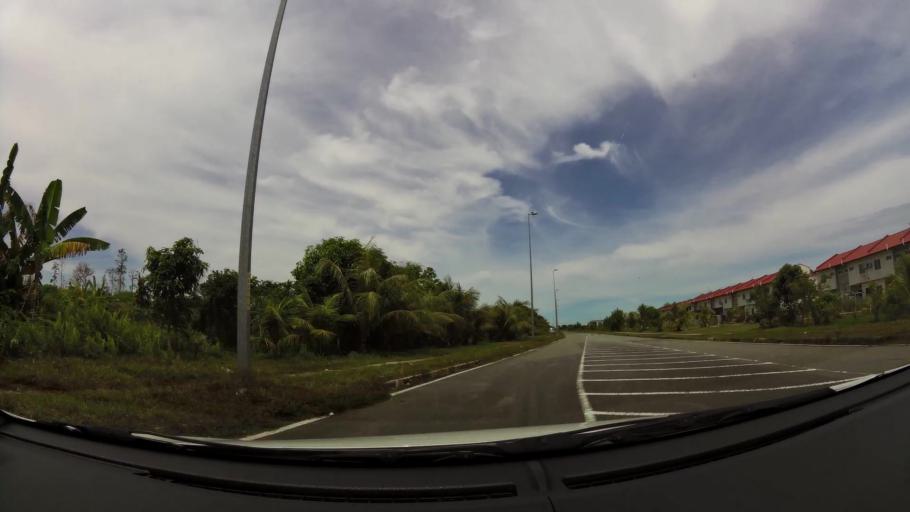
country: BN
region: Belait
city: Kuala Belait
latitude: 4.5871
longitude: 114.2707
